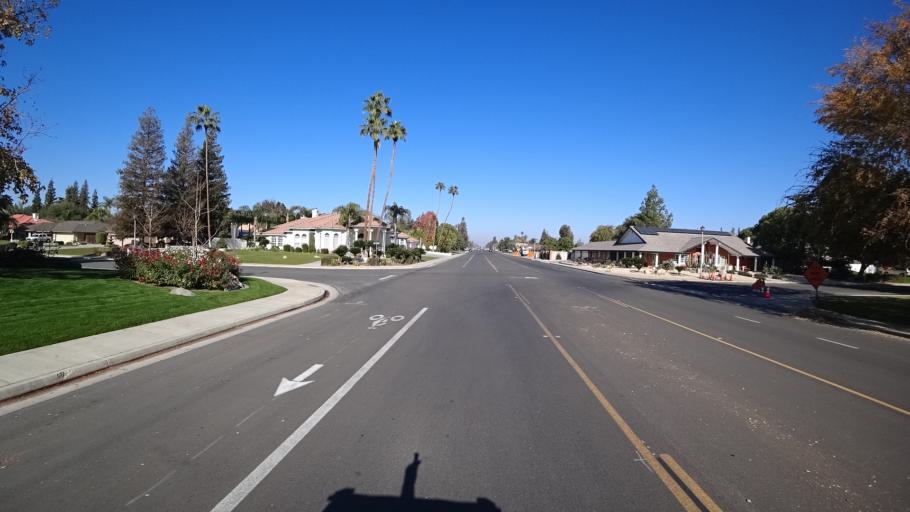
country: US
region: California
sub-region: Kern County
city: Rosedale
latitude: 35.3731
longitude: -119.1368
